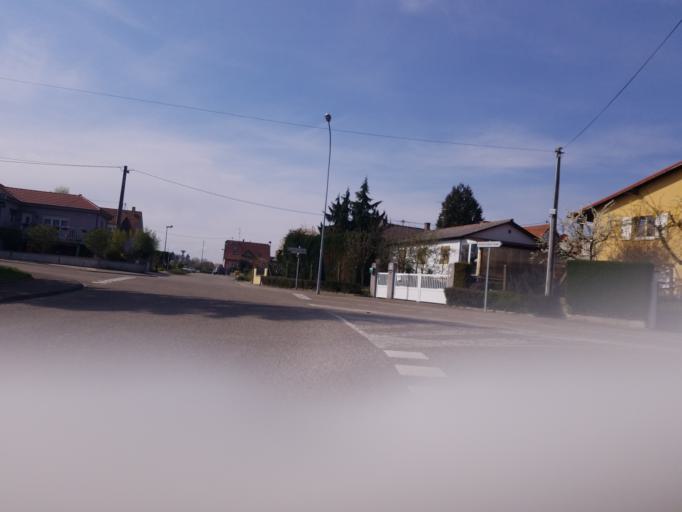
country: FR
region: Alsace
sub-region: Departement du Bas-Rhin
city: Betschdorf
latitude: 48.9011
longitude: 7.9709
